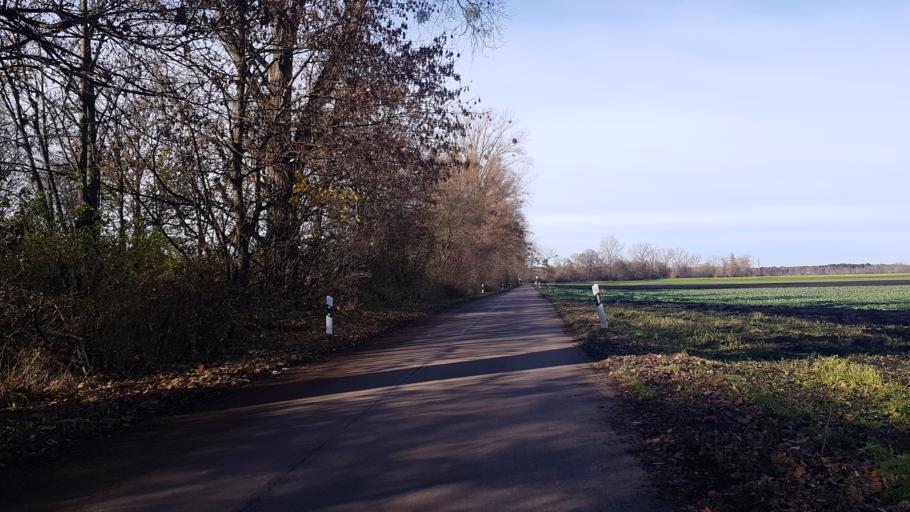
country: DE
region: Bavaria
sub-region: Upper Bavaria
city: Karlsfeld
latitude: 48.2284
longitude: 11.5094
